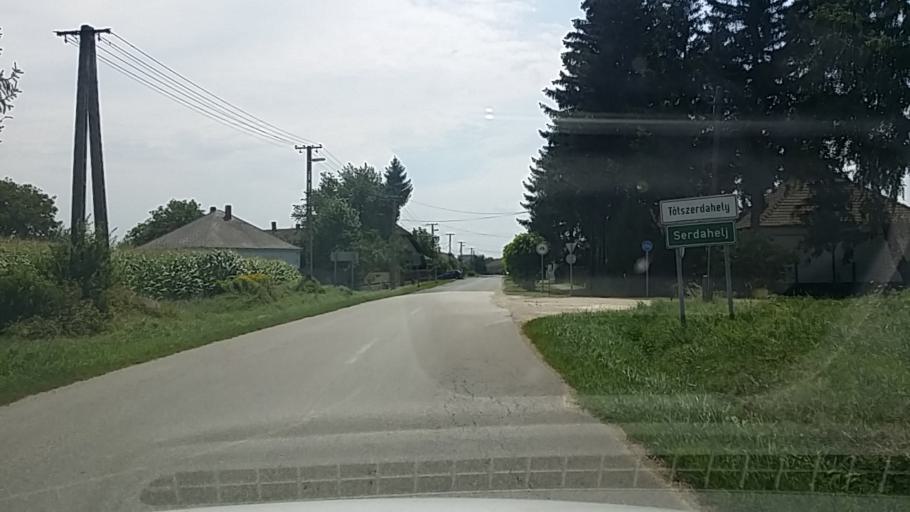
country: HU
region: Zala
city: Becsehely
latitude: 46.4042
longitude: 16.7887
